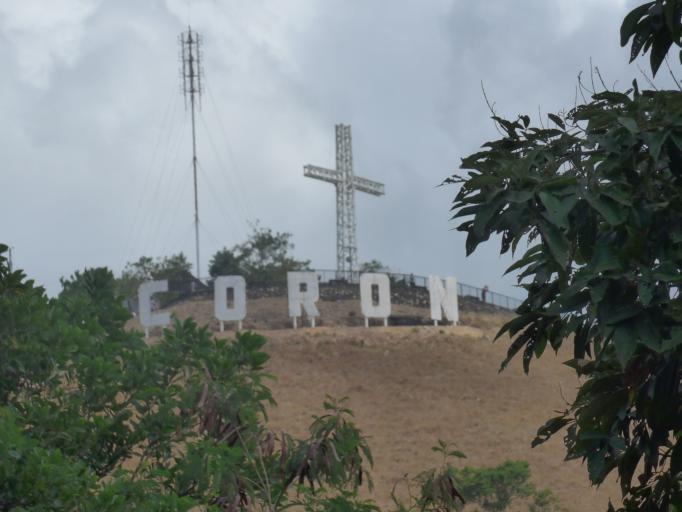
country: PH
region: Mimaropa
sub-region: Province of Palawan
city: Coron
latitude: 12.0011
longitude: 120.2036
